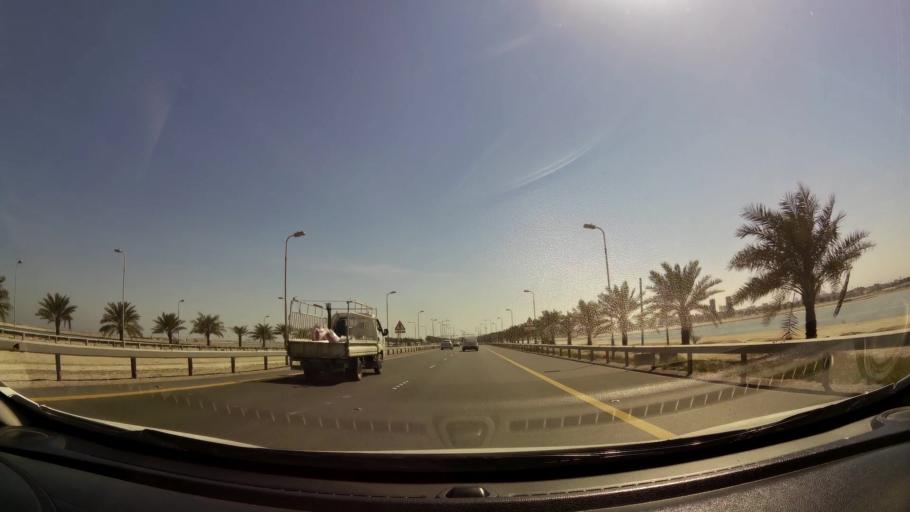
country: BH
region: Muharraq
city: Al Hadd
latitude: 26.2575
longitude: 50.6602
